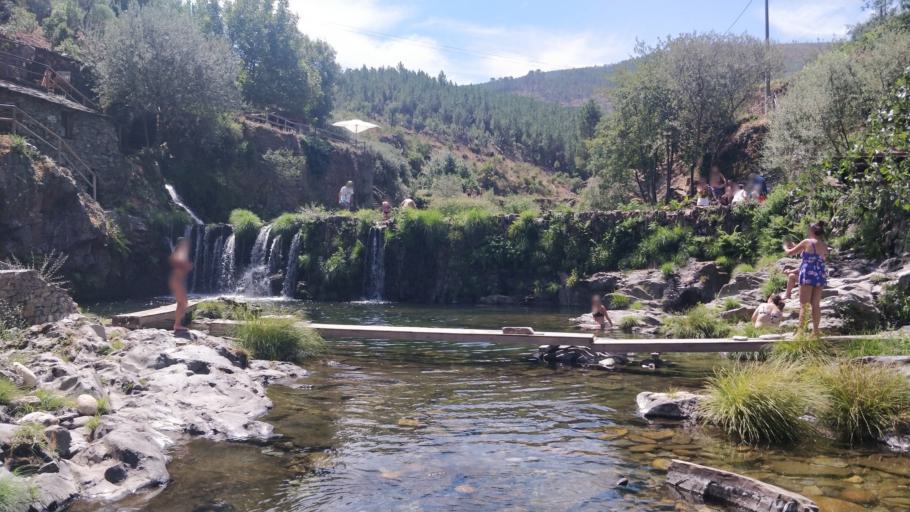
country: PT
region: Coimbra
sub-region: Oliveira do Hospital
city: Oliveira do Hospital
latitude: 40.2933
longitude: -7.7536
